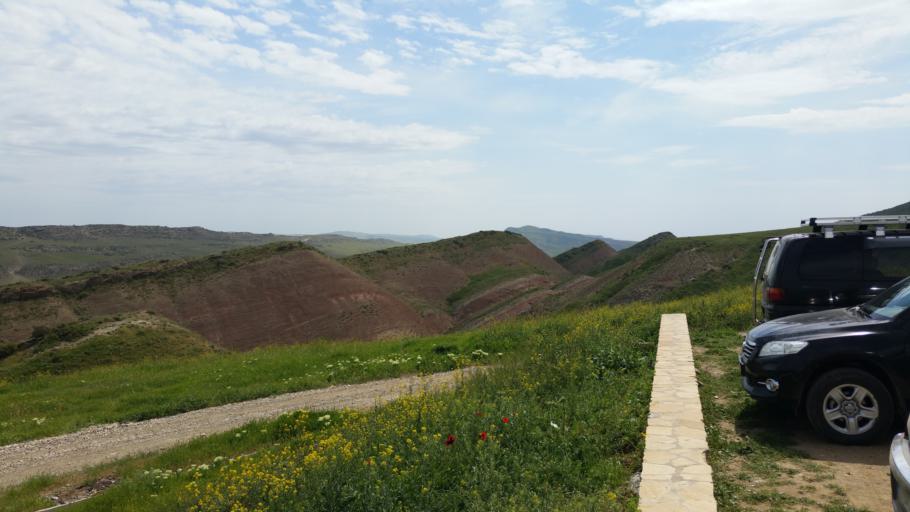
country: AZ
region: Agstafa
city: Saloglu
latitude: 41.4488
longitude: 45.3767
